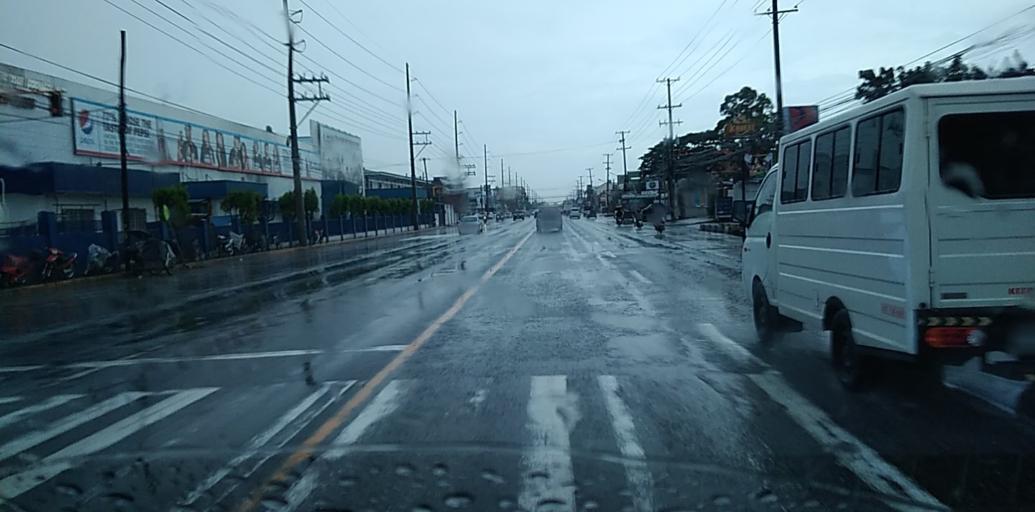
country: PH
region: Central Luzon
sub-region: Province of Pampanga
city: Bulaon
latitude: 15.0697
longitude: 120.6478
